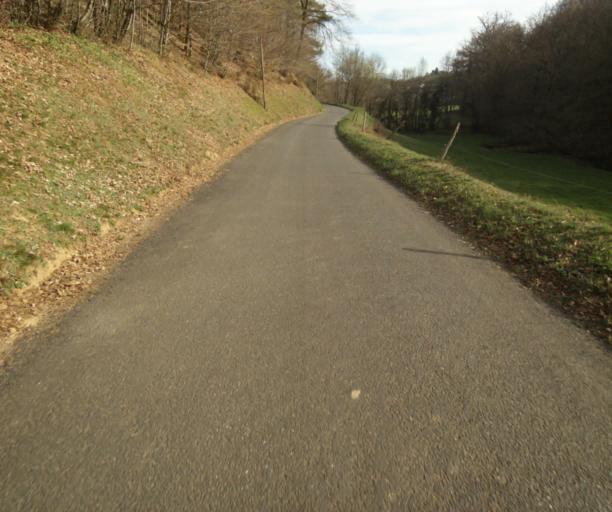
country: FR
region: Limousin
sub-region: Departement de la Correze
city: Naves
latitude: 45.2961
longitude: 1.7561
